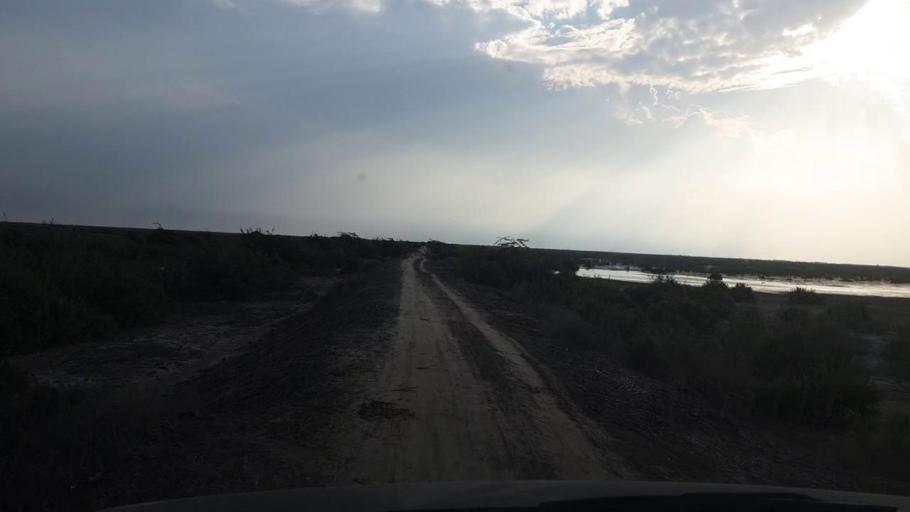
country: PK
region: Sindh
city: Badin
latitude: 24.4385
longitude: 68.6742
